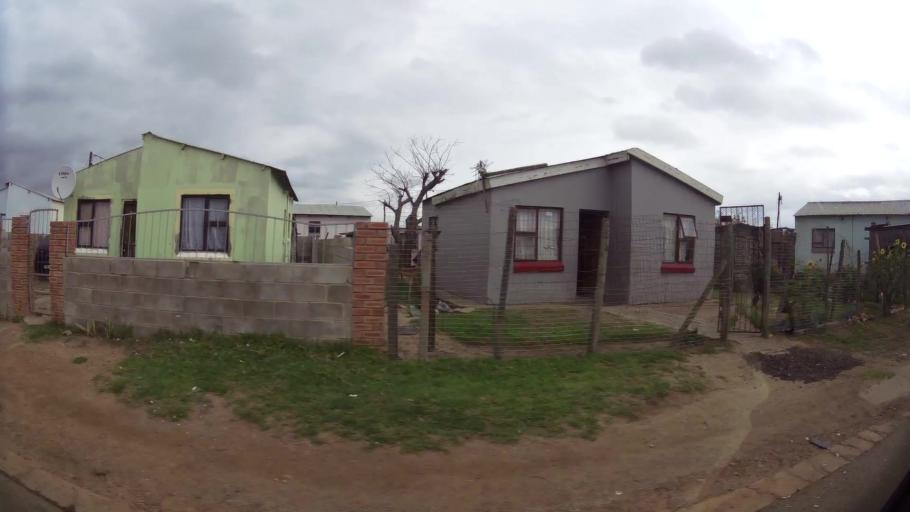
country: ZA
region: Eastern Cape
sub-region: Nelson Mandela Bay Metropolitan Municipality
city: Port Elizabeth
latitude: -33.8886
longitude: 25.5542
